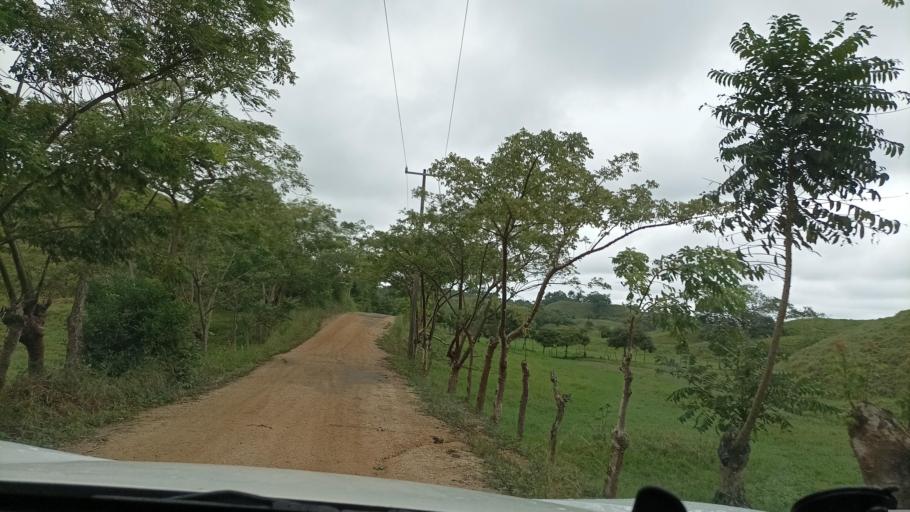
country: MX
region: Veracruz
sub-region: Moloacan
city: Cuichapa
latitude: 17.7913
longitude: -94.3820
